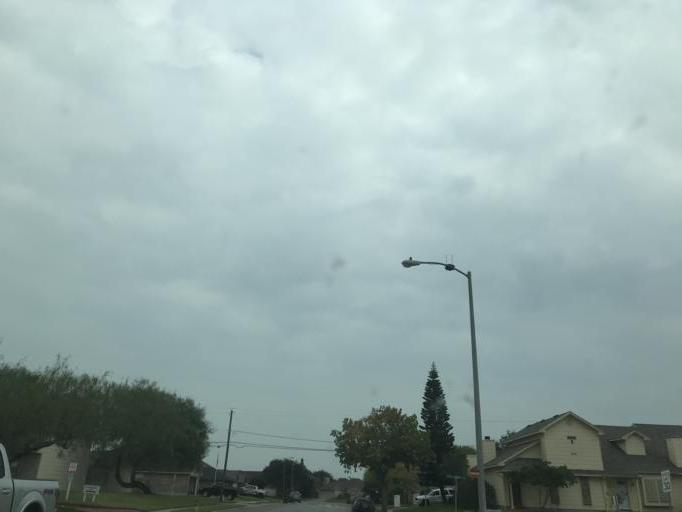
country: US
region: Texas
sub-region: Nueces County
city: Corpus Christi
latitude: 27.6687
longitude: -97.3532
